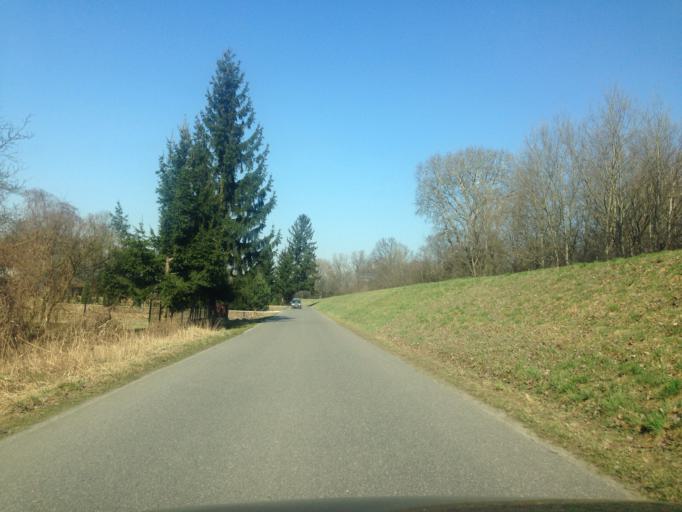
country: PL
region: Masovian Voivodeship
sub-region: Powiat piaseczynski
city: Konstancin-Jeziorna
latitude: 52.1233
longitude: 21.1732
